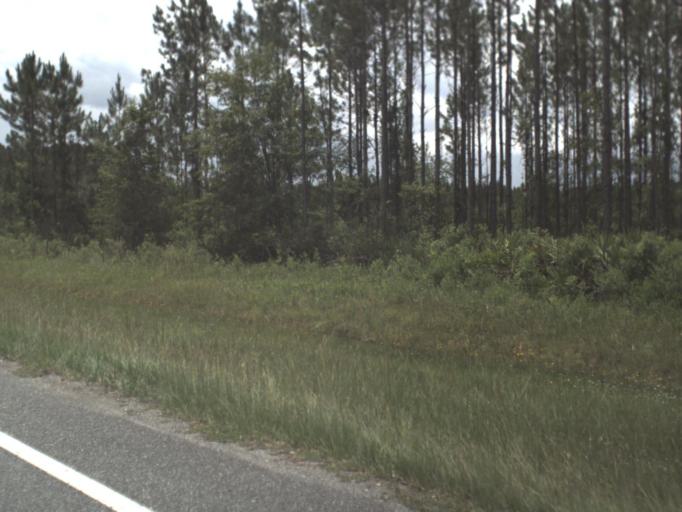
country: US
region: Florida
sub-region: Union County
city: Lake Butler
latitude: 29.9812
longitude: -82.2396
